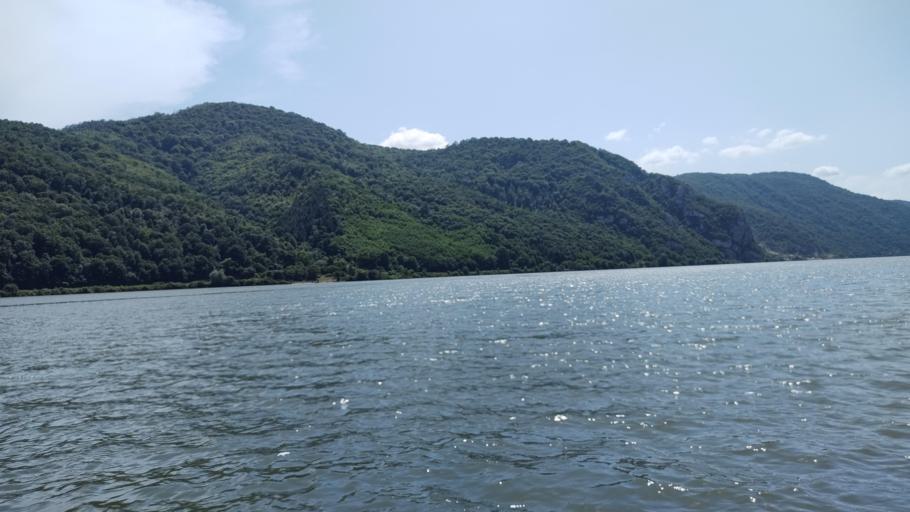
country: RO
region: Caras-Severin
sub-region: Comuna Pescari
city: Coronini
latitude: 44.6584
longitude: 21.7554
